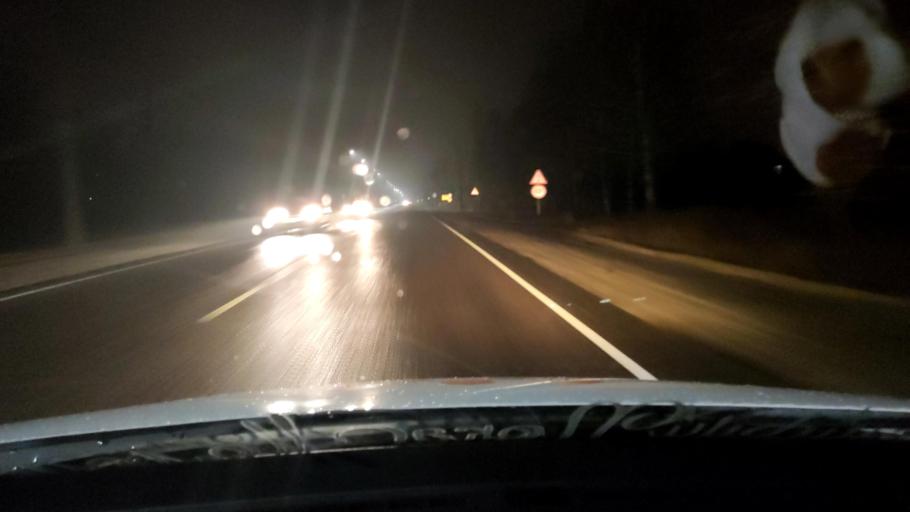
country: RU
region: Voronezj
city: Semiluki
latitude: 51.7079
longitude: 39.0228
